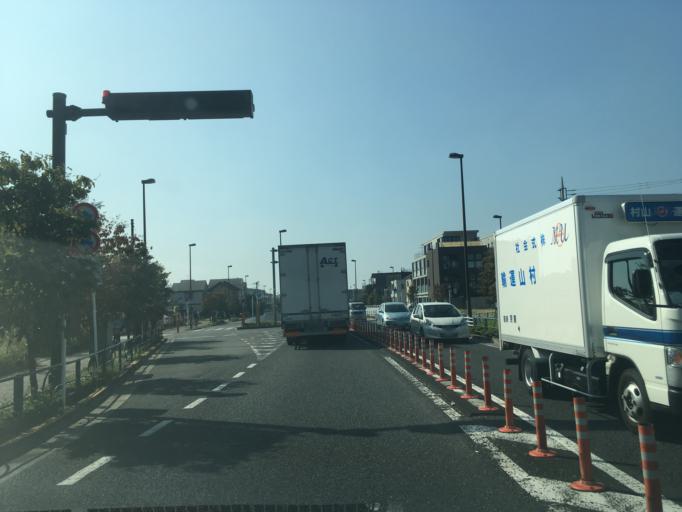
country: JP
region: Tokyo
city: Hino
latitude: 35.7102
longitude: 139.3786
